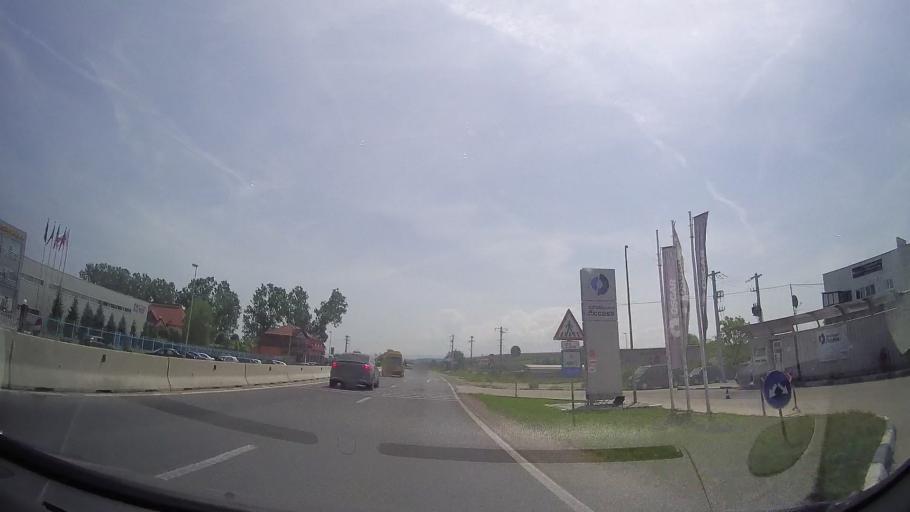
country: RO
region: Hunedoara
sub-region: Municipiul Deva
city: Cristur
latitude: 45.8541
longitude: 22.9627
